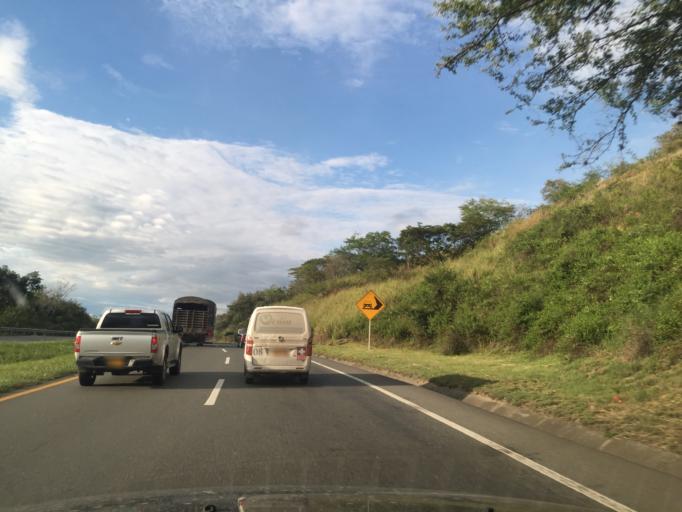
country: CO
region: Valle del Cauca
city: Bugalagrande
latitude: 4.2027
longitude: -76.1536
